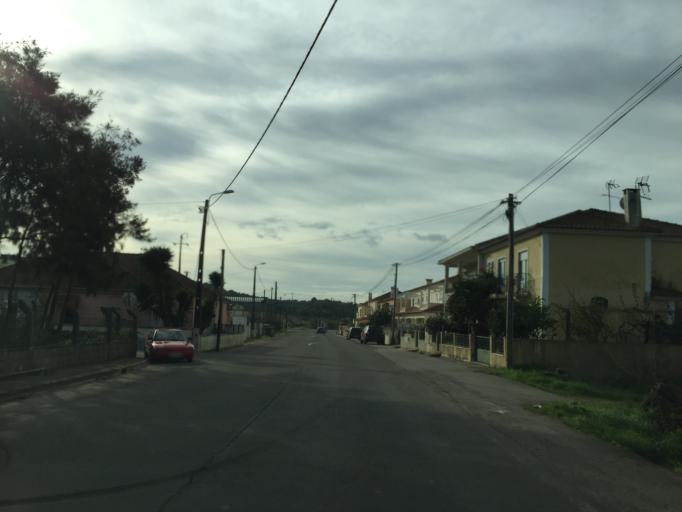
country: PT
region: Lisbon
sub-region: Sintra
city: Pero Pinheiro
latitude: 38.8671
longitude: -9.2990
